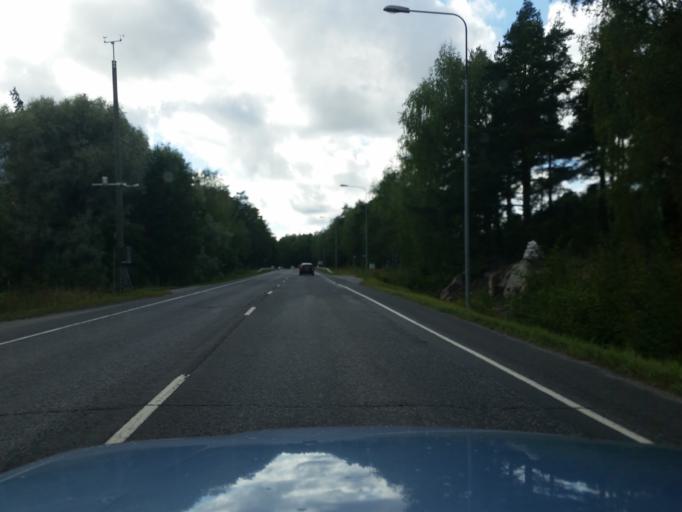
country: FI
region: Varsinais-Suomi
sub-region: Aboland-Turunmaa
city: Pargas
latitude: 60.3144
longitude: 22.3258
